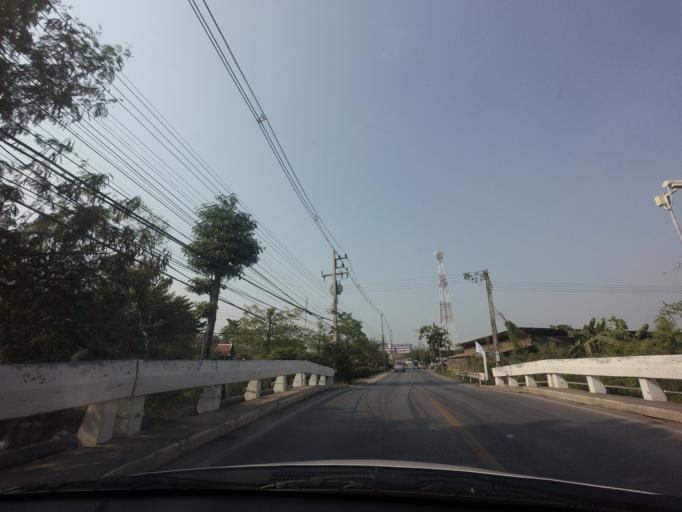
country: TH
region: Nakhon Pathom
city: Sam Phran
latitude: 13.7183
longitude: 100.2053
